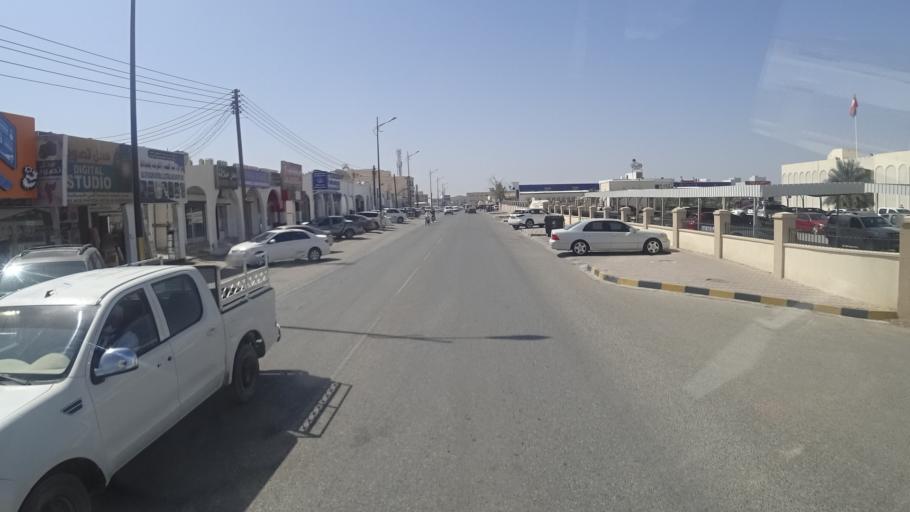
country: OM
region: Ash Sharqiyah
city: Ibra'
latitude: 22.6954
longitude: 58.5458
